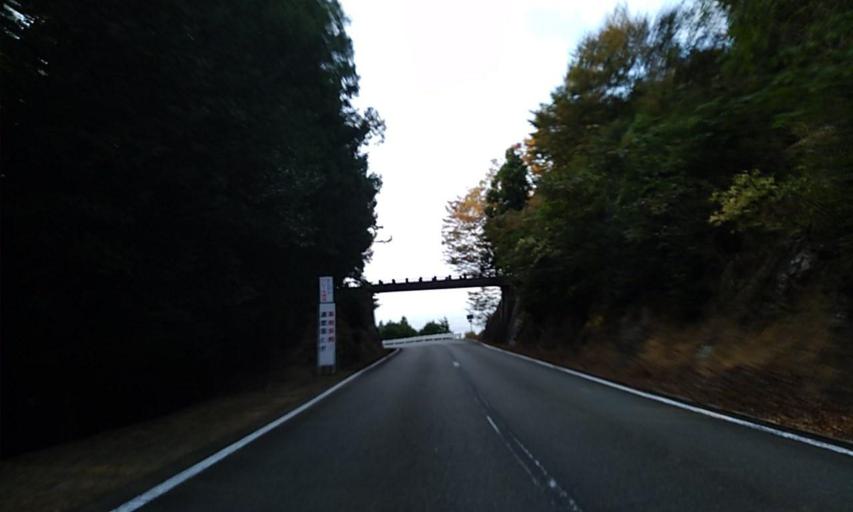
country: JP
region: Mie
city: Ise
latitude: 34.4598
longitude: 136.7641
